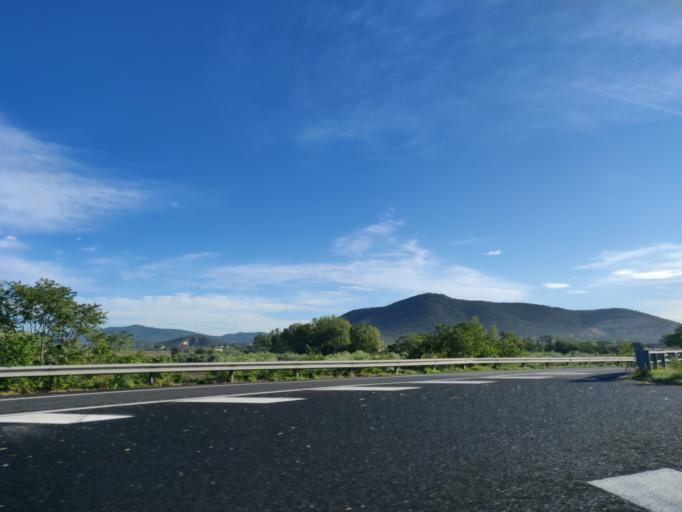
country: IT
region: Tuscany
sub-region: Provincia di Grosseto
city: Bagno Roselle
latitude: 42.7970
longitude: 11.1258
